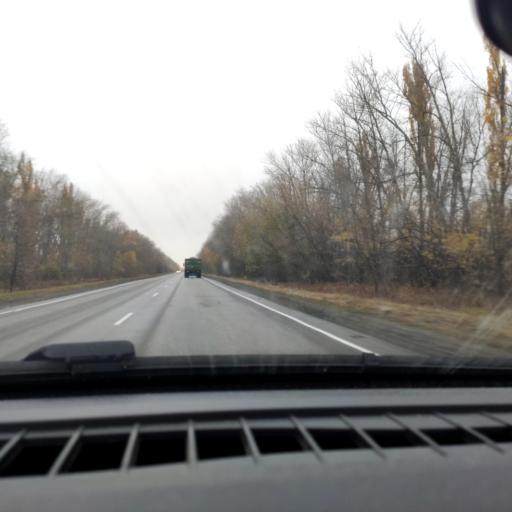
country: RU
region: Voronezj
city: Ostrogozhsk
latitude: 50.9609
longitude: 39.0242
